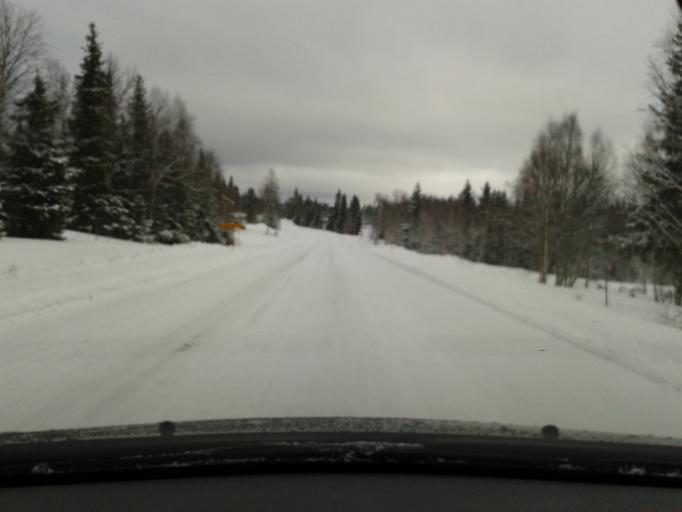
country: SE
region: Vaesterbotten
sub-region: Vilhelmina Kommun
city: Sjoberg
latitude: 65.2427
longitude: 15.7542
